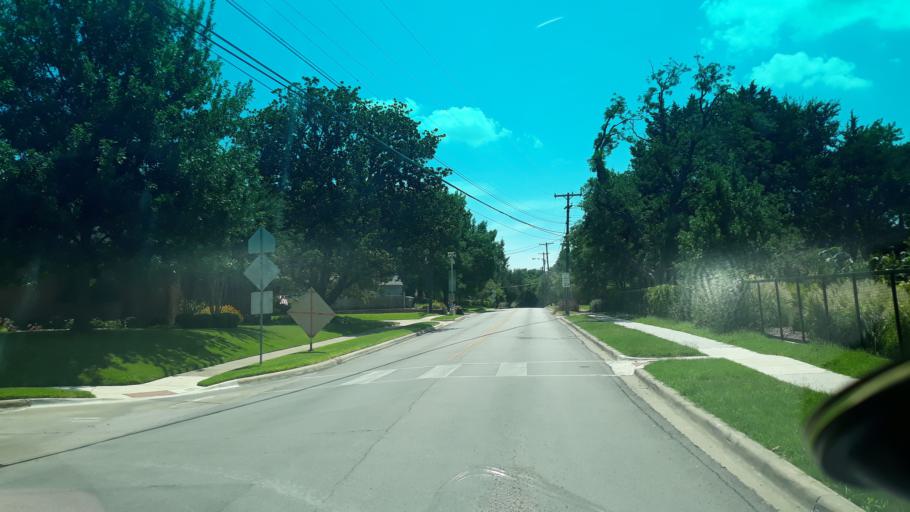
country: US
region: Texas
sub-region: Dallas County
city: Highland Park
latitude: 32.8244
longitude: -96.7412
